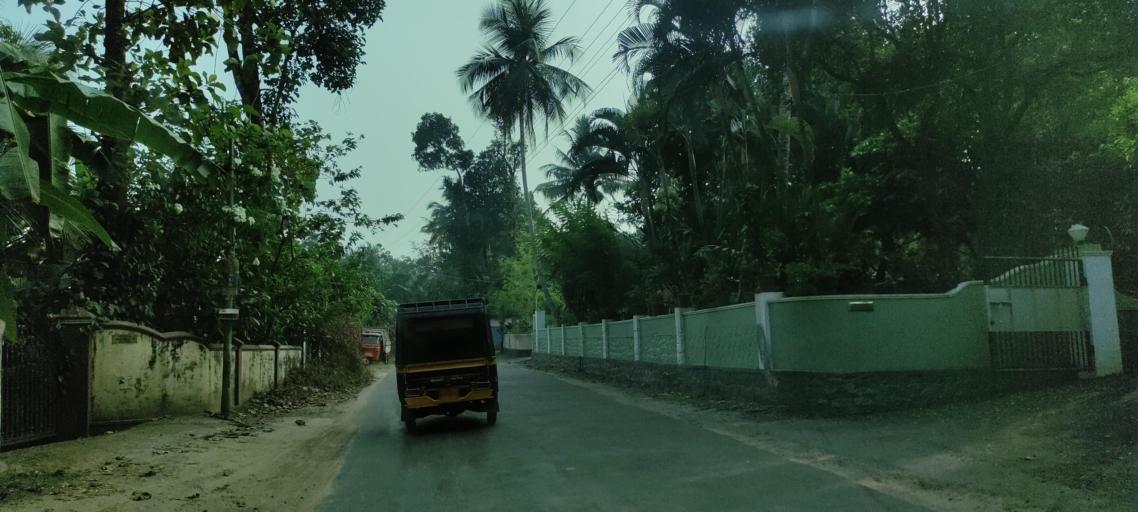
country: IN
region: Kerala
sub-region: Kottayam
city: Vaikam
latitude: 9.7556
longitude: 76.4918
